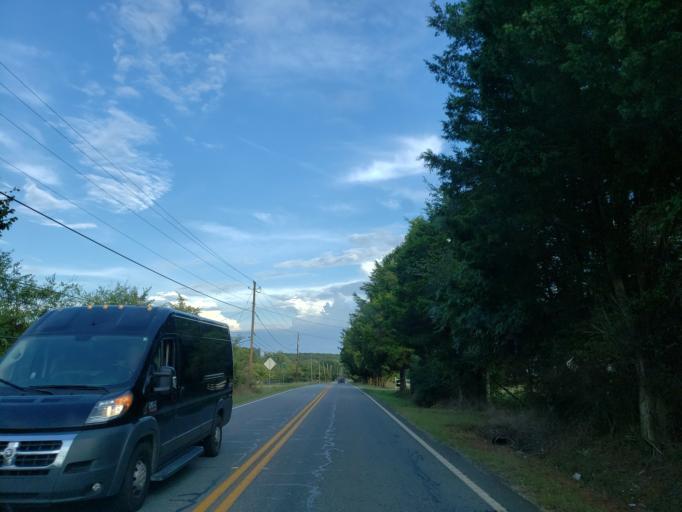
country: US
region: Georgia
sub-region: Bartow County
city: Cartersville
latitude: 34.2323
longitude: -84.8638
